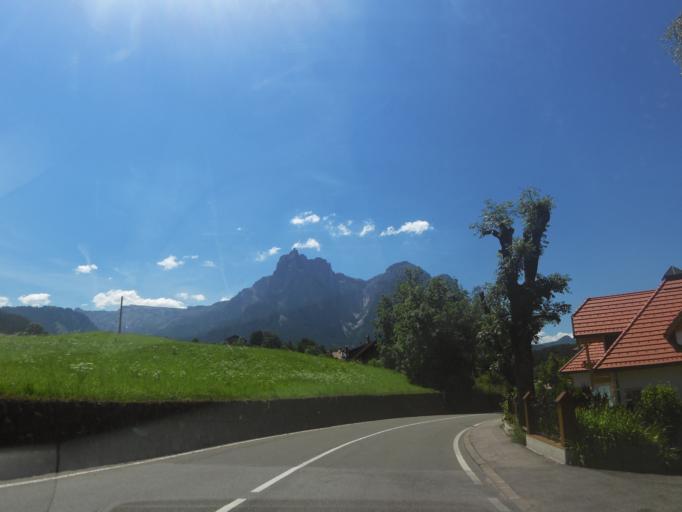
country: IT
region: Trentino-Alto Adige
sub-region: Bolzano
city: Castelrotto
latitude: 46.5626
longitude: 11.5572
